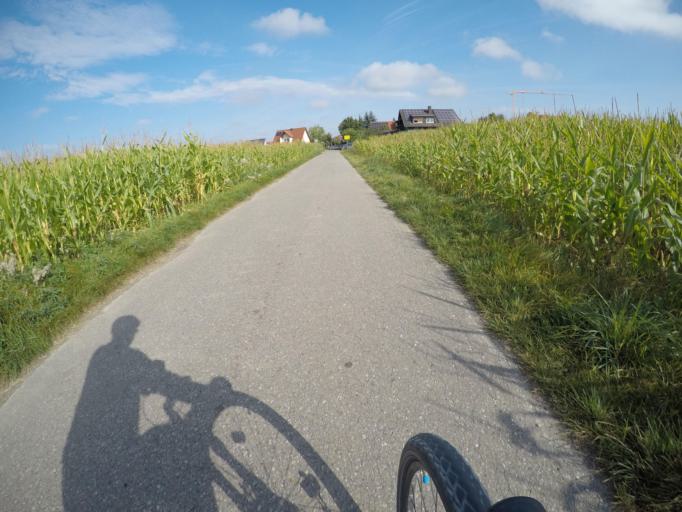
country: DE
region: Bavaria
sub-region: Swabia
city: Nordendorf
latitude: 48.5870
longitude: 10.8350
